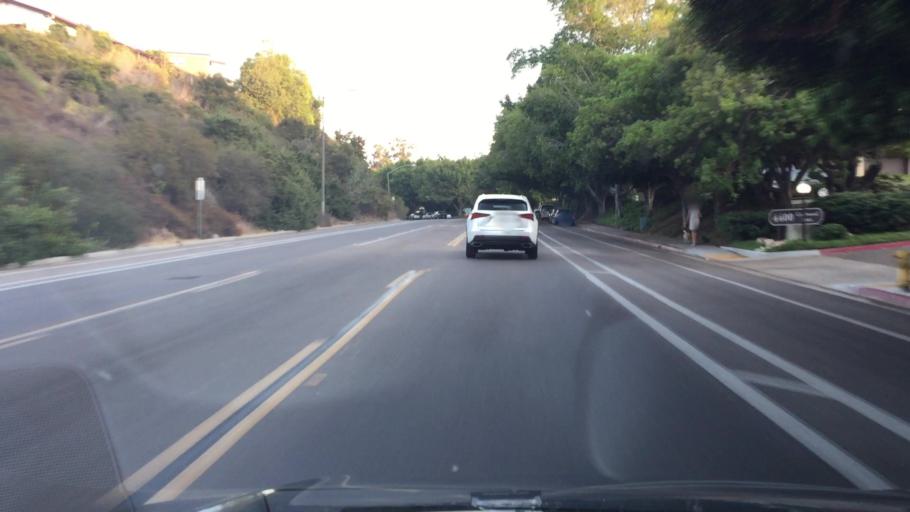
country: US
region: California
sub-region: San Diego County
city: Lemon Grove
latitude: 32.7645
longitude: -117.0835
